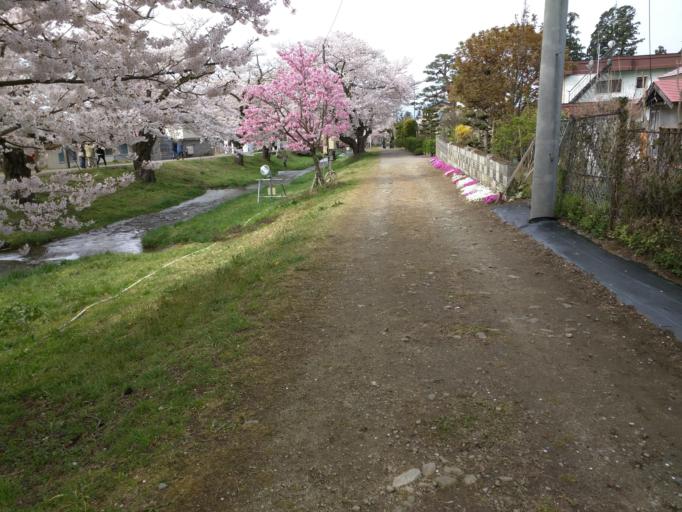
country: JP
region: Fukushima
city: Inawashiro
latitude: 37.5381
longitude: 140.1393
